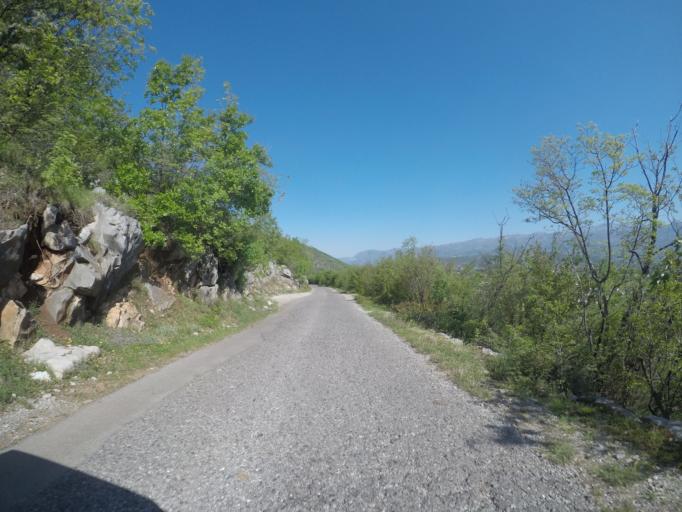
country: ME
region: Danilovgrad
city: Danilovgrad
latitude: 42.5277
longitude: 19.0939
